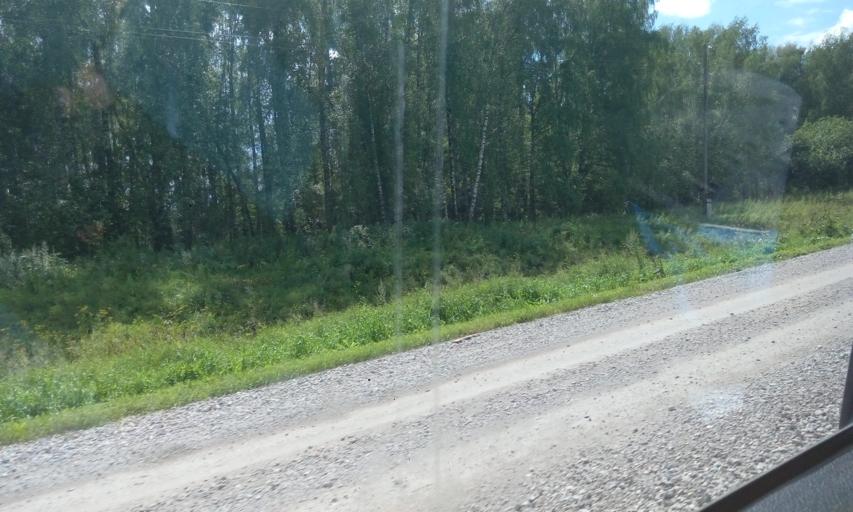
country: RU
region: Novosibirsk
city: Iskitim
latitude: 54.6981
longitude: 83.3913
